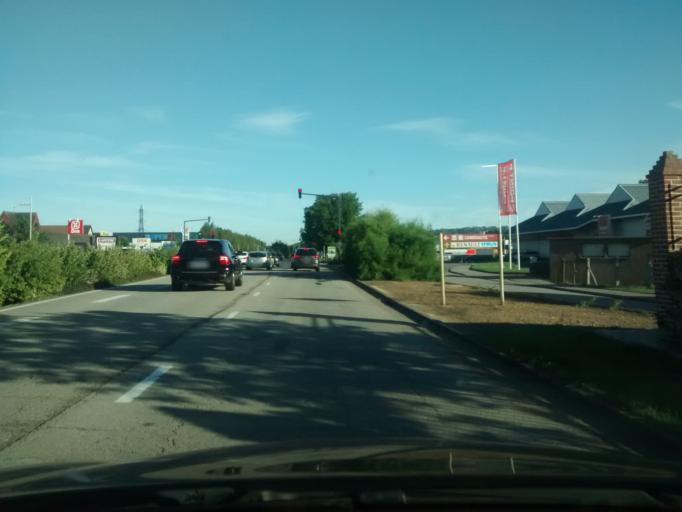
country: FR
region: Lower Normandy
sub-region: Departement du Calvados
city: Touques
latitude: 49.3432
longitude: 0.1005
